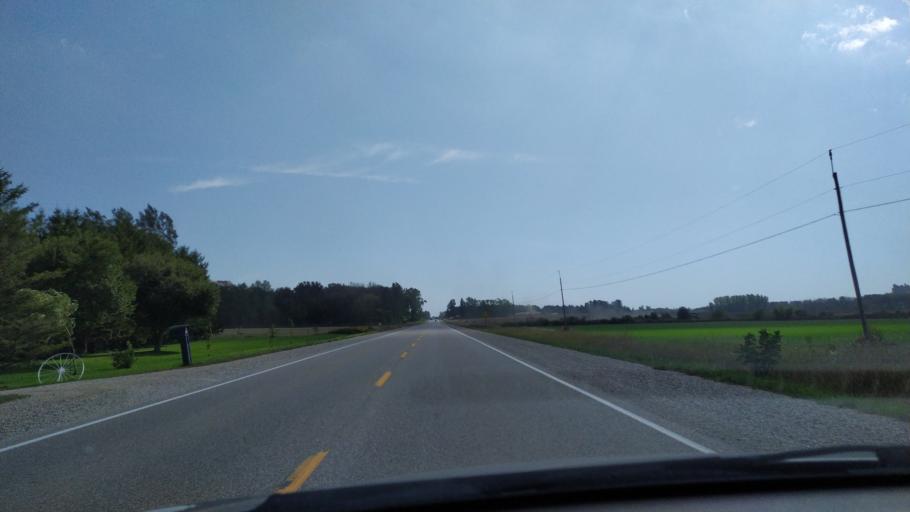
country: CA
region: Ontario
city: Ingersoll
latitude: 43.1108
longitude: -80.8791
